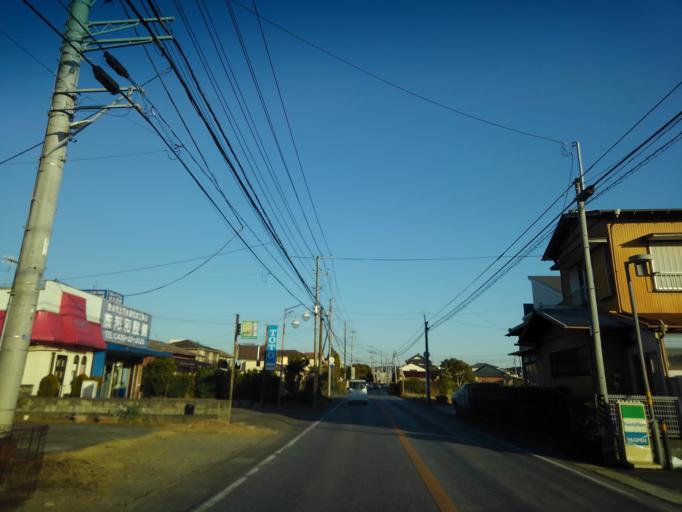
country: JP
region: Chiba
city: Kimitsu
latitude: 35.3063
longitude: 139.9534
